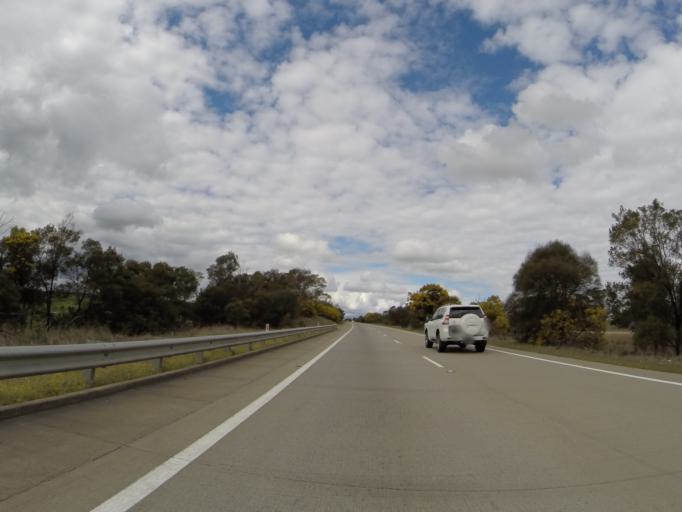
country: AU
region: New South Wales
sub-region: Yass Valley
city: Gundaroo
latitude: -34.8213
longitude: 149.3604
